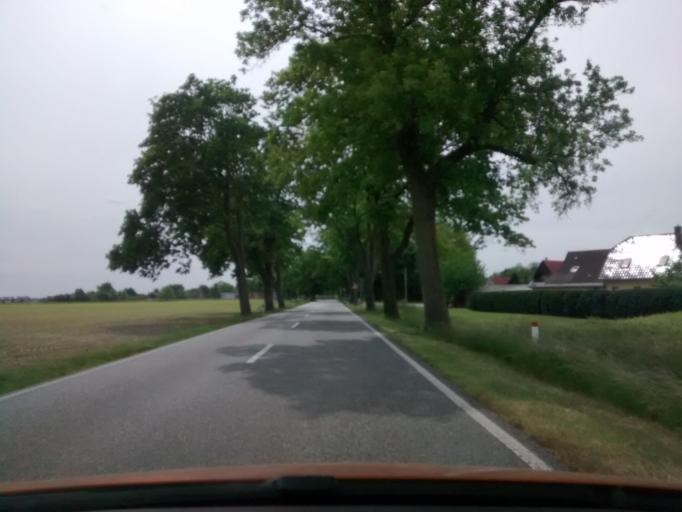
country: DE
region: Brandenburg
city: Juterbog
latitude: 51.9355
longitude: 13.1208
